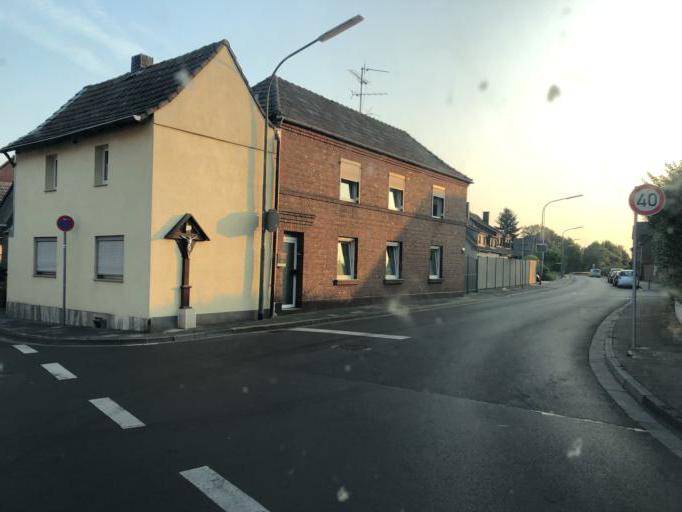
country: DE
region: North Rhine-Westphalia
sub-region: Regierungsbezirk Dusseldorf
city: Neubrueck
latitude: 51.1724
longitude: 6.6361
